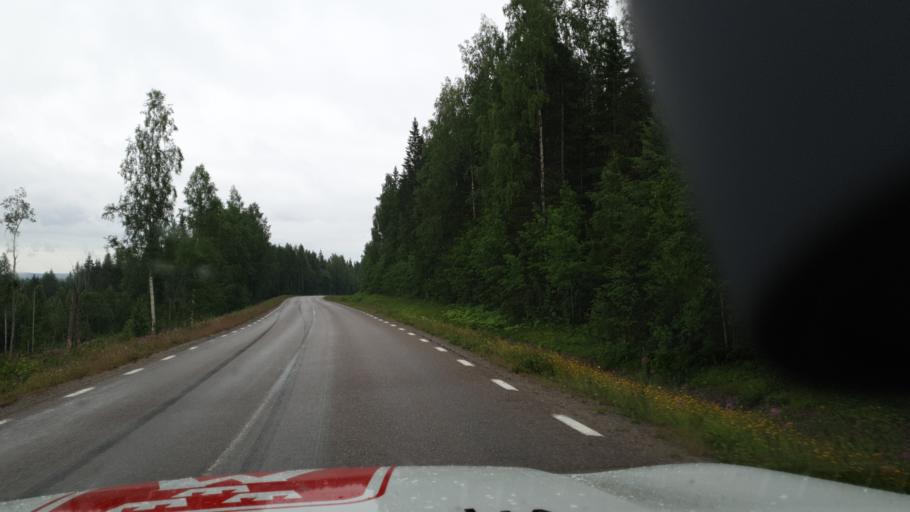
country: SE
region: Vaesterbotten
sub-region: Vannas Kommun
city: Vaennaes
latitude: 63.7914
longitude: 19.8183
